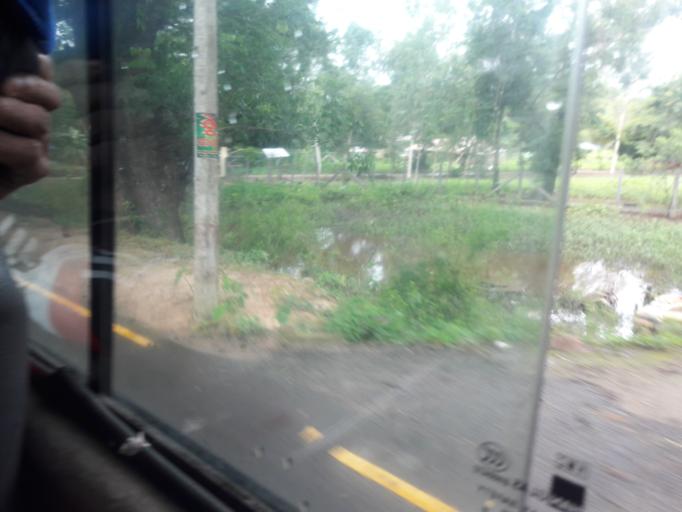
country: MM
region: Bago
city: Nyaunglebin
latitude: 17.7759
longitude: 96.6467
